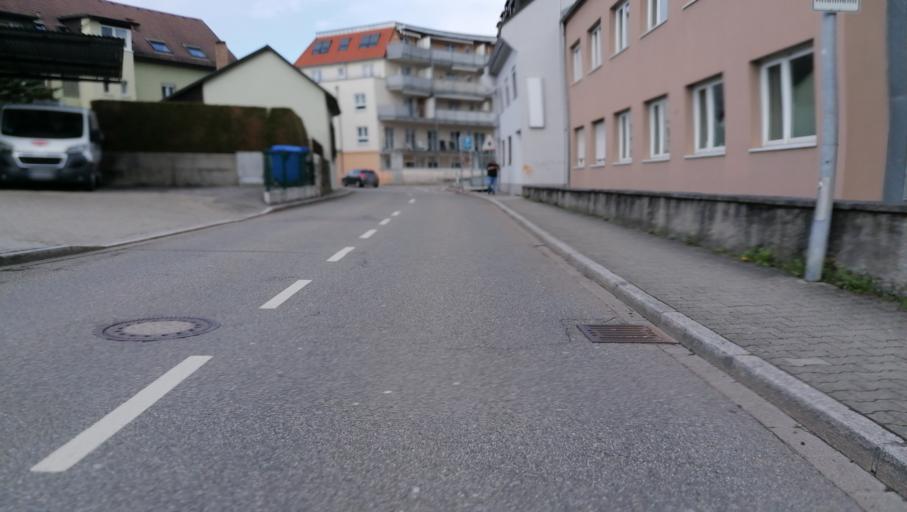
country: DE
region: Baden-Wuerttemberg
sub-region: Freiburg Region
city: Bad Sackingen
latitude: 47.5533
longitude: 7.9457
